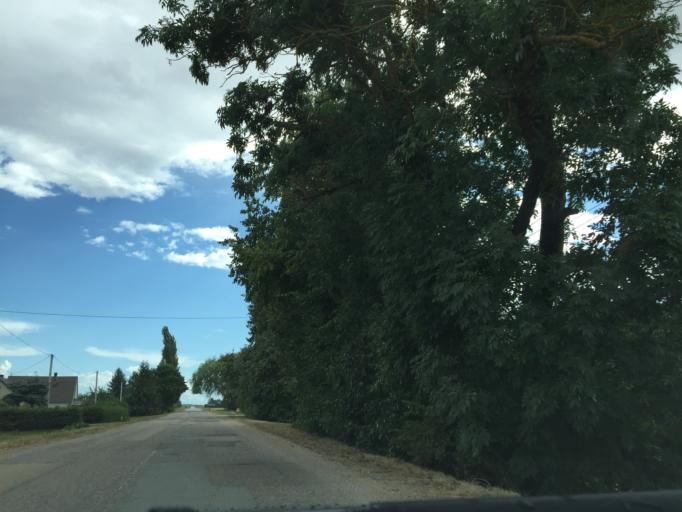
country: LT
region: Siauliu apskritis
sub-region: Joniskis
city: Joniskis
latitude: 56.3092
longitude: 23.5530
